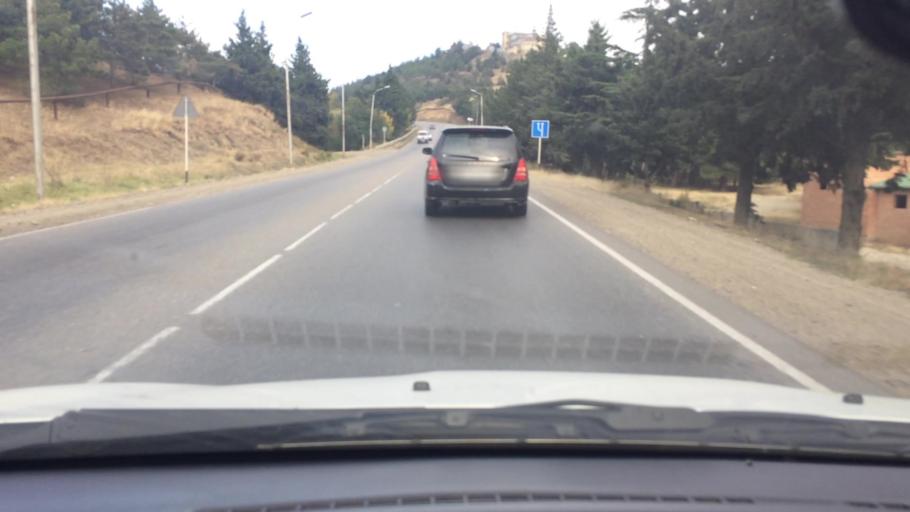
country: GE
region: T'bilisi
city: Tbilisi
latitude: 41.6209
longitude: 44.7967
